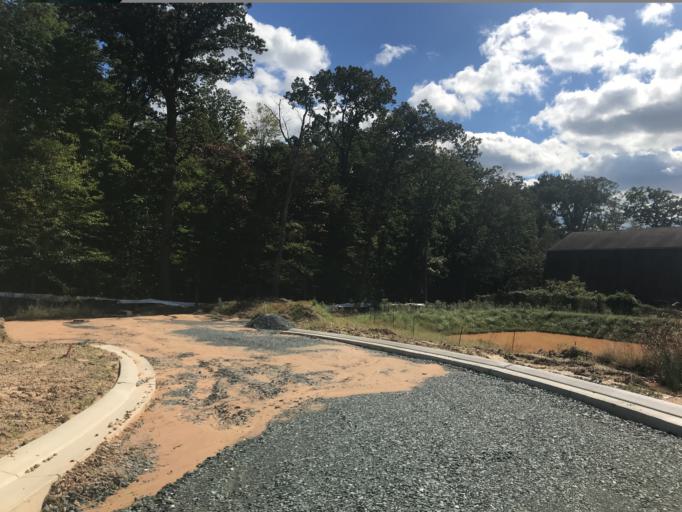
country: US
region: Maryland
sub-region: Baltimore County
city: Overlea
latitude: 39.3657
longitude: -76.4975
